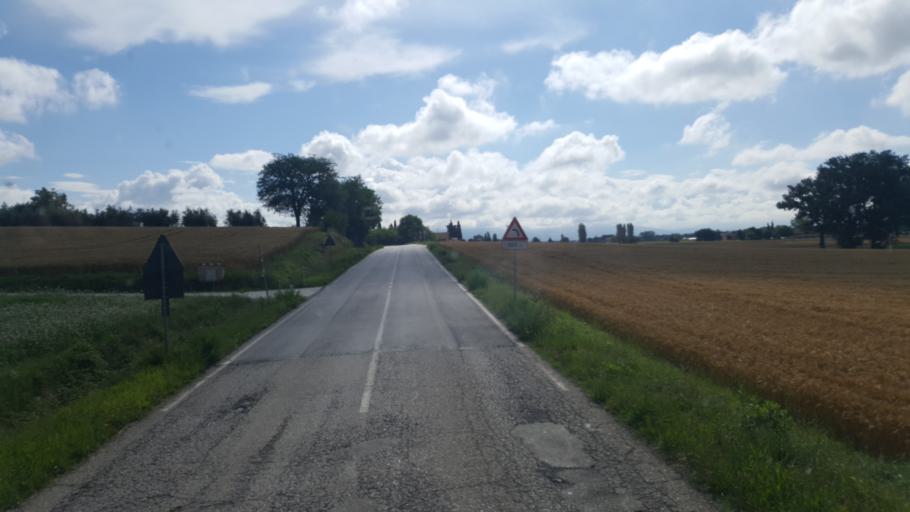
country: IT
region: Umbria
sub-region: Provincia di Perugia
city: Torgiano
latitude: 43.0375
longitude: 12.4628
